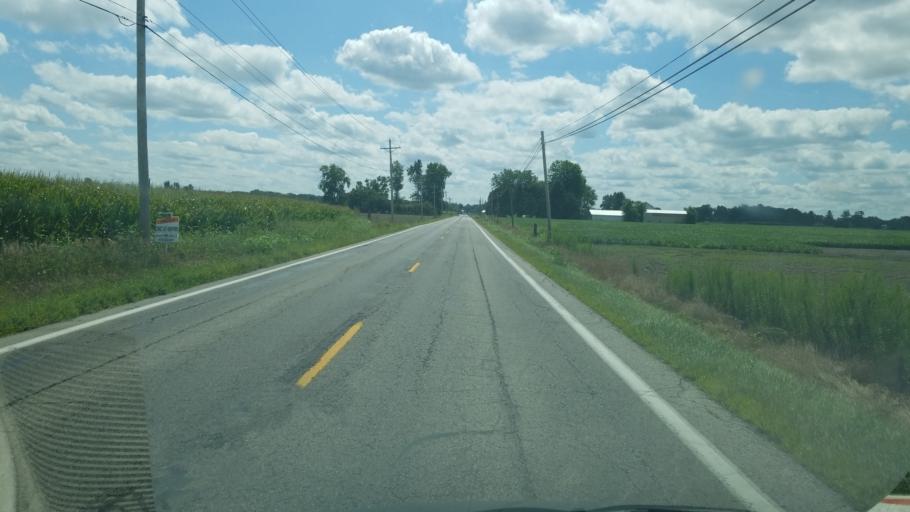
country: US
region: Ohio
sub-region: Henry County
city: Liberty Center
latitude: 41.4655
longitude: -84.0088
